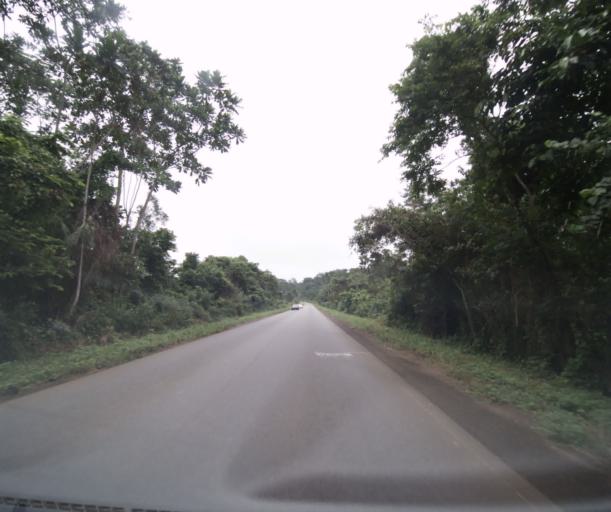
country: CM
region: Littoral
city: Edea
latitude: 3.6703
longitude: 10.1109
